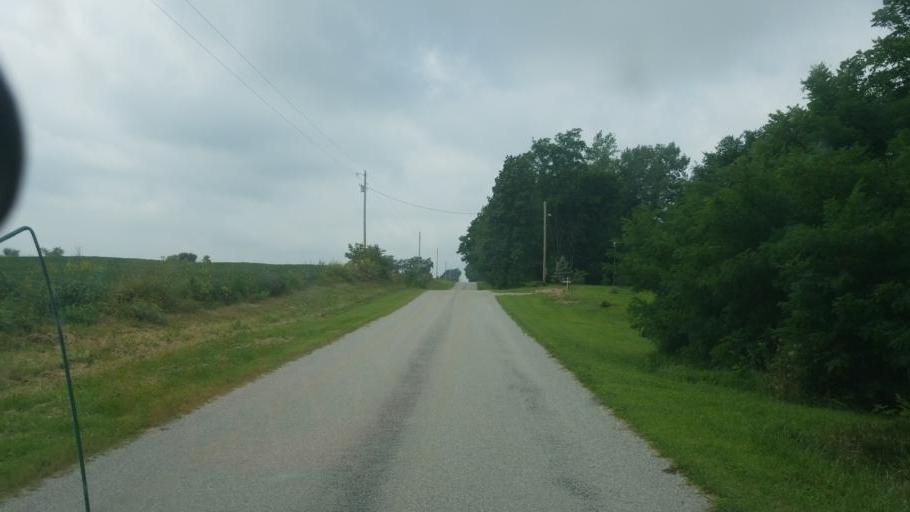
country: US
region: Ohio
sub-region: Huron County
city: Greenwich
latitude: 41.0107
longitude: -82.4920
